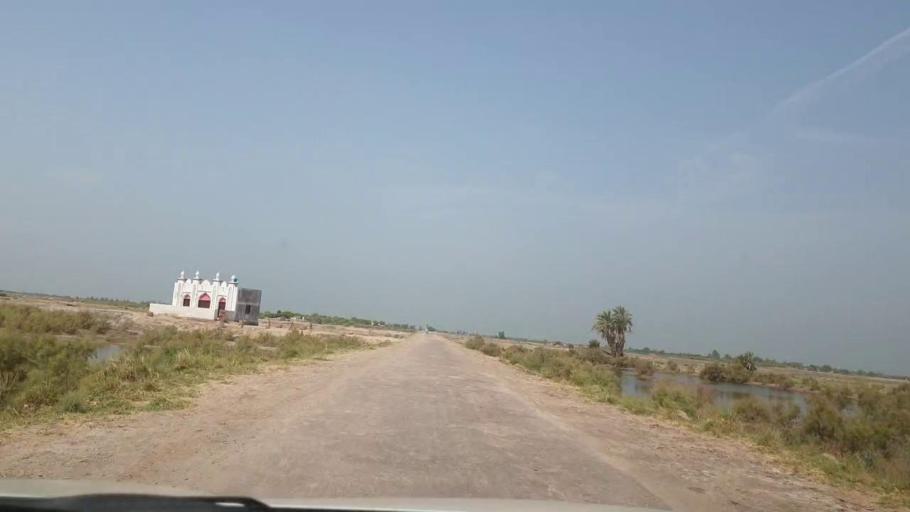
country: PK
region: Sindh
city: Larkana
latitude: 27.4311
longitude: 68.2139
